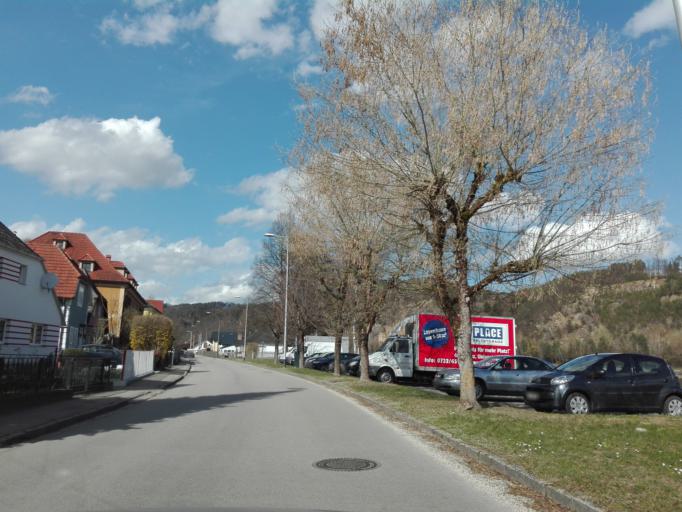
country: AT
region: Upper Austria
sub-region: Politischer Bezirk Urfahr-Umgebung
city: Feldkirchen an der Donau
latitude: 48.3722
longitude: 14.0282
